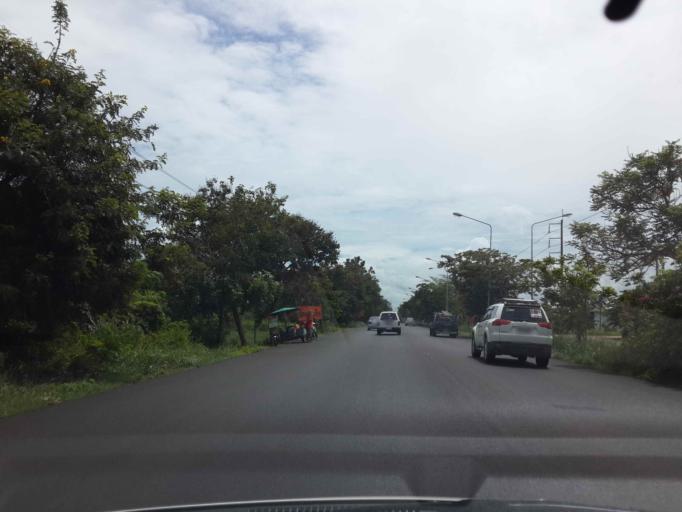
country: TH
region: Ratchaburi
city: Pak Tho
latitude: 13.4445
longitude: 99.8029
